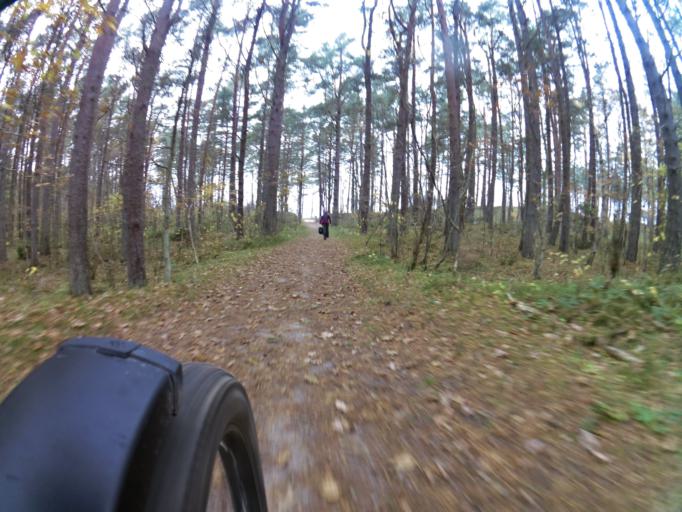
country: PL
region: Pomeranian Voivodeship
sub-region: Powiat pucki
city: Krokowa
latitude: 54.8306
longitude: 18.1248
